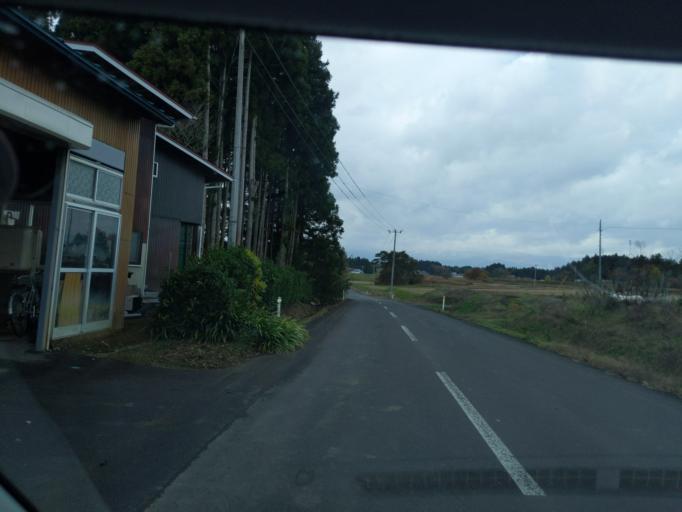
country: JP
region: Iwate
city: Mizusawa
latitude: 39.0700
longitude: 141.0754
